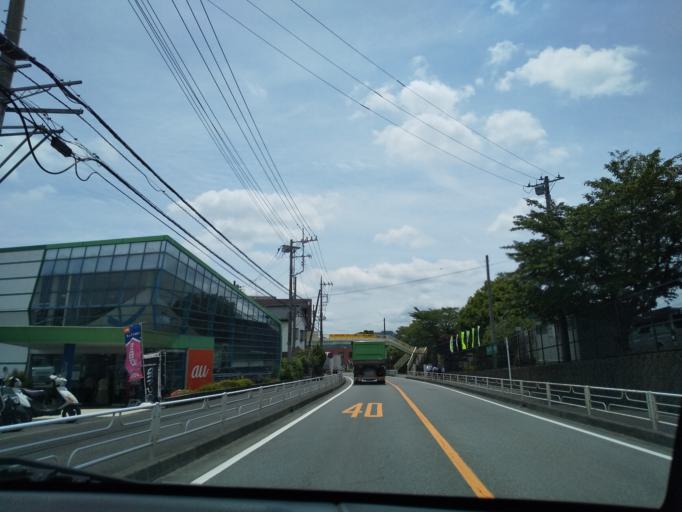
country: JP
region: Tokyo
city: Hachioji
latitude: 35.5968
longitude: 139.3025
